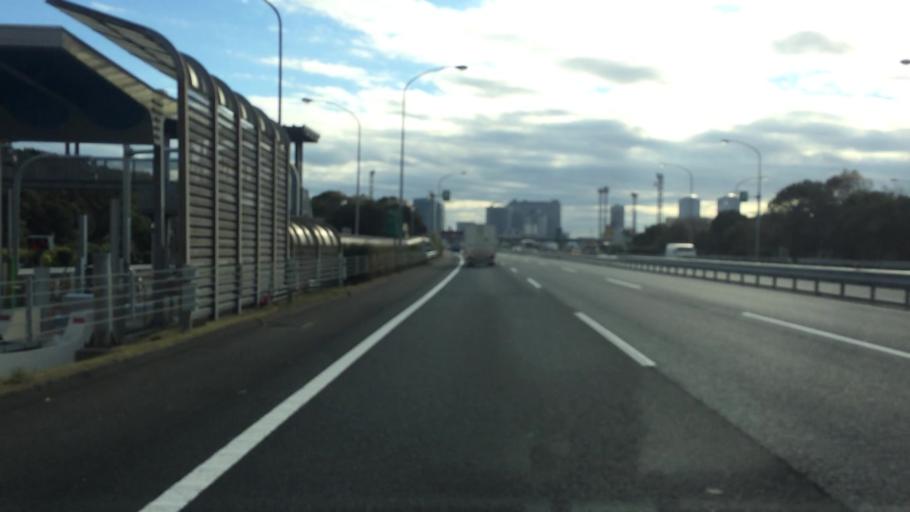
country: JP
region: Chiba
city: Funabashi
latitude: 35.6632
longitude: 140.0213
